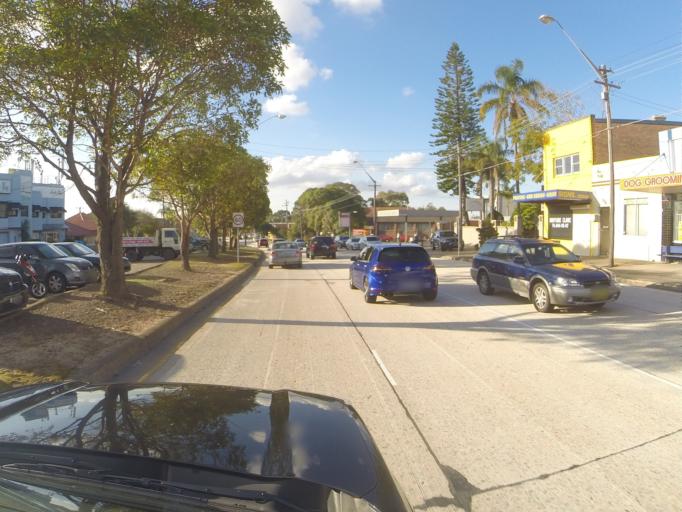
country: AU
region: New South Wales
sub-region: Rockdale
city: Bexley
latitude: -33.9598
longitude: 151.1172
